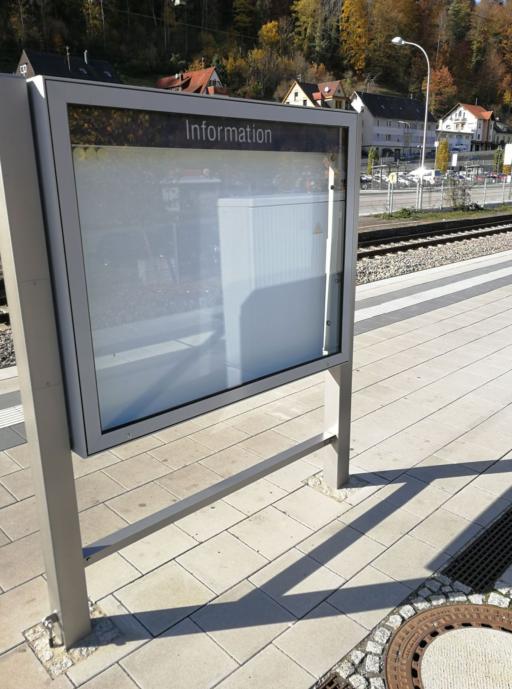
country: DE
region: Baden-Wuerttemberg
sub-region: Freiburg Region
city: Oberndorf
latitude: 48.2959
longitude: 8.5755
